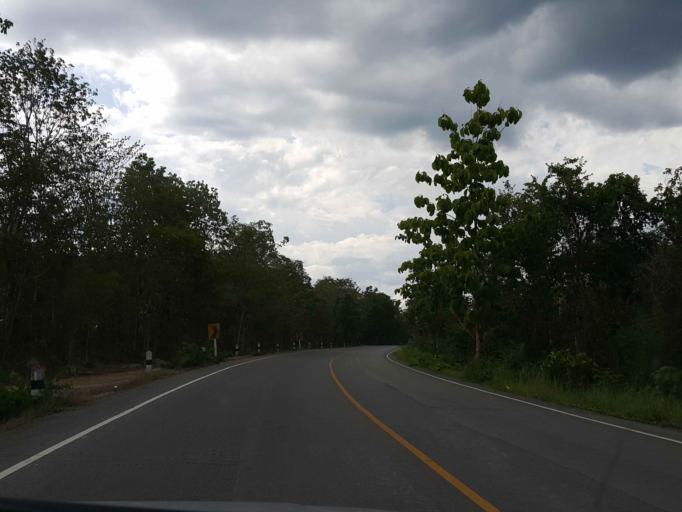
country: TH
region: Sukhothai
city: Thung Saliam
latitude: 17.3780
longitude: 99.4011
